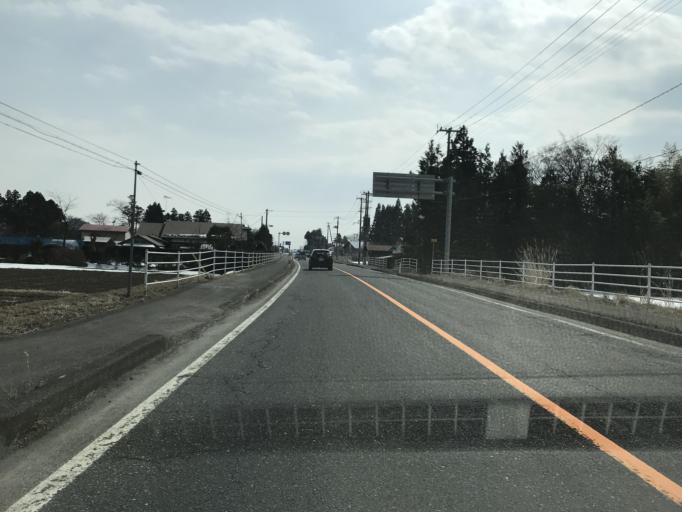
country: JP
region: Miyagi
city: Furukawa
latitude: 38.7006
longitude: 140.8401
